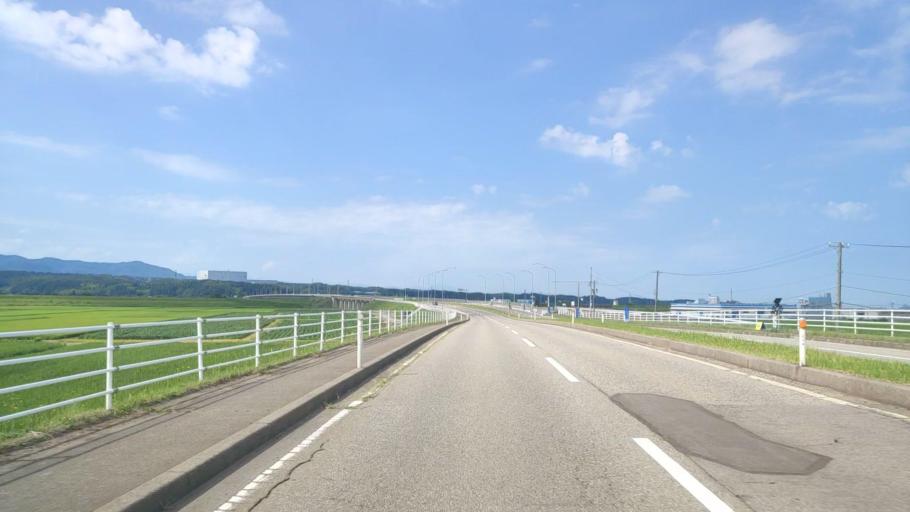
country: JP
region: Ishikawa
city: Matsuto
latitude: 36.4665
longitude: 136.5787
